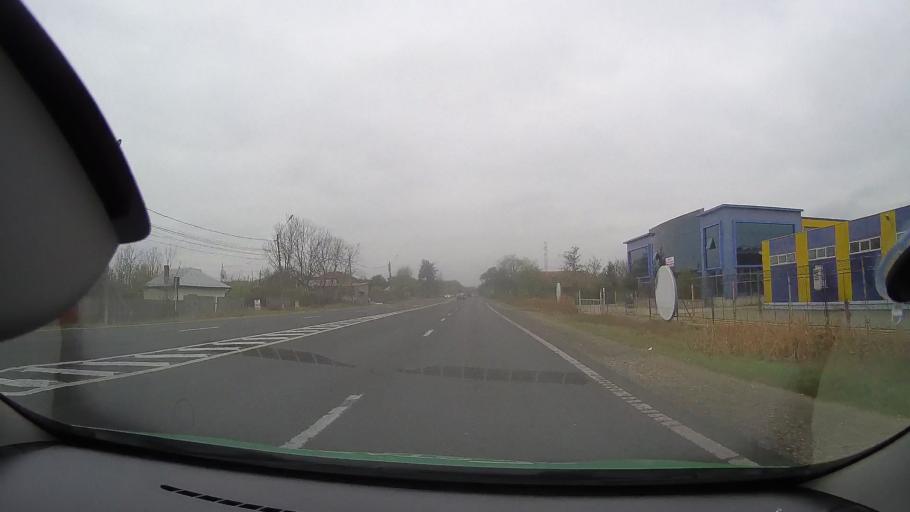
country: RO
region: Ilfov
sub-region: Comuna Ciolpani
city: Ciolpani
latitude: 44.7135
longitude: 26.0987
